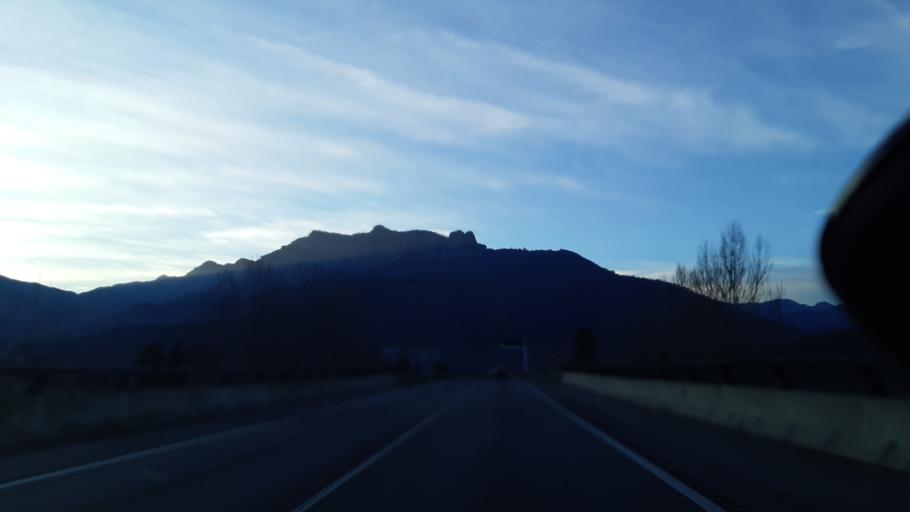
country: ES
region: Catalonia
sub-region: Provincia de Girona
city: Bas
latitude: 42.1287
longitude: 2.4482
